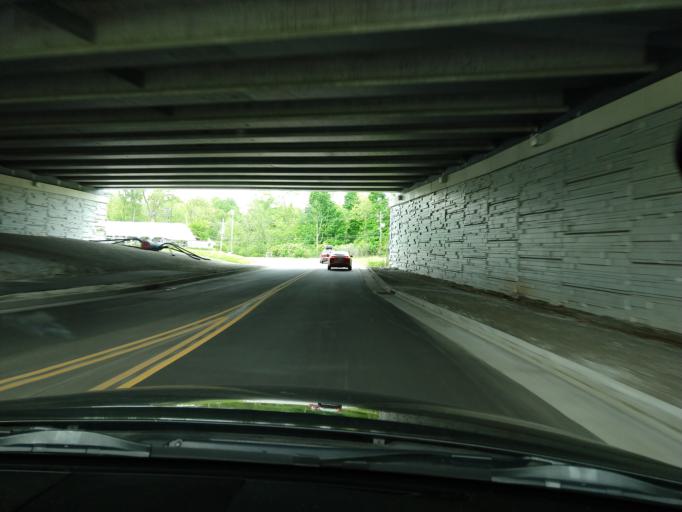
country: US
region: Indiana
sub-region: Hamilton County
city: Westfield
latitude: 40.0120
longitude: -86.1285
